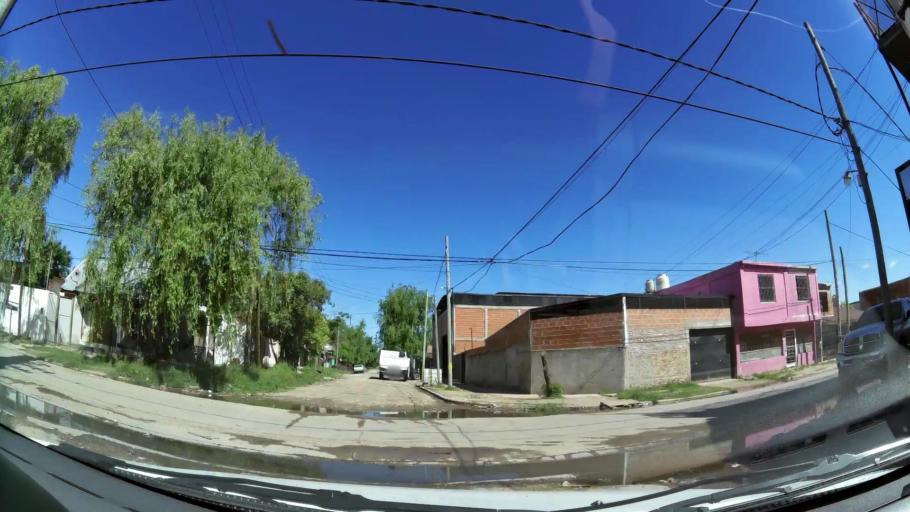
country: AR
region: Buenos Aires
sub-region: Partido de General San Martin
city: General San Martin
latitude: -34.5159
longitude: -58.5840
